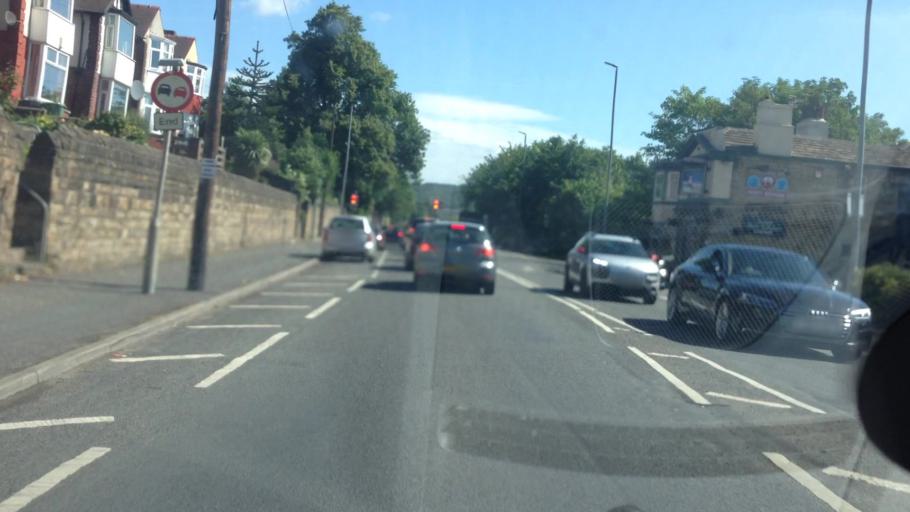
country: GB
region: England
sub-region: Kirklees
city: Dewsbury
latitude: 53.6851
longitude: -1.6445
